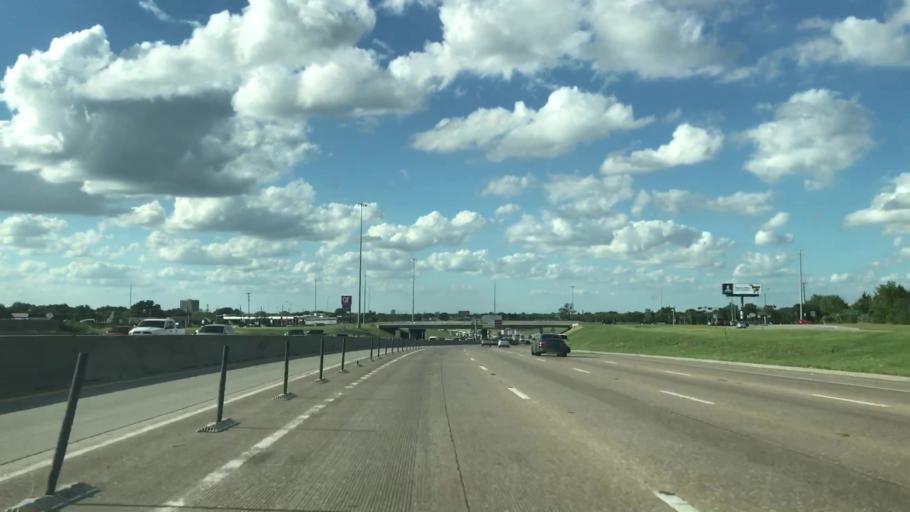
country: US
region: Texas
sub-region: Dallas County
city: Richardson
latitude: 32.8921
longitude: -96.7098
